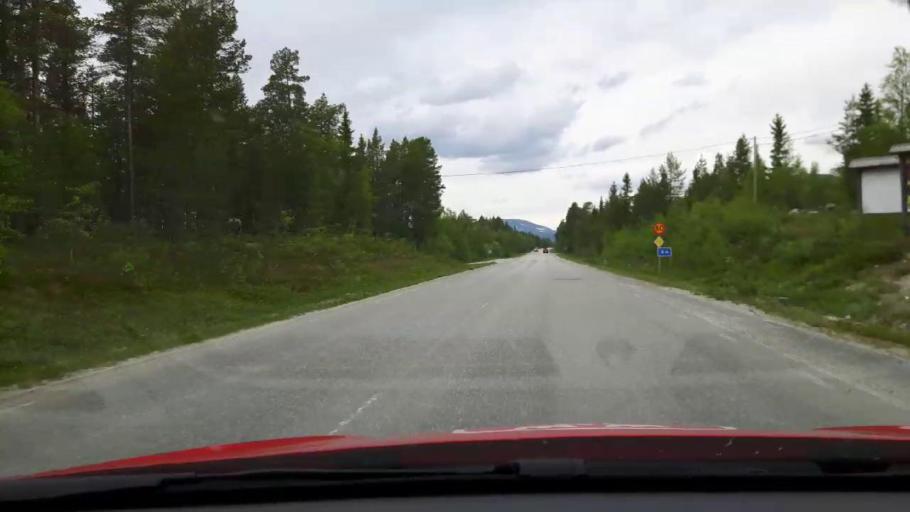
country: NO
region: Hedmark
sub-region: Engerdal
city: Engerdal
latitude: 62.5237
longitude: 12.5874
